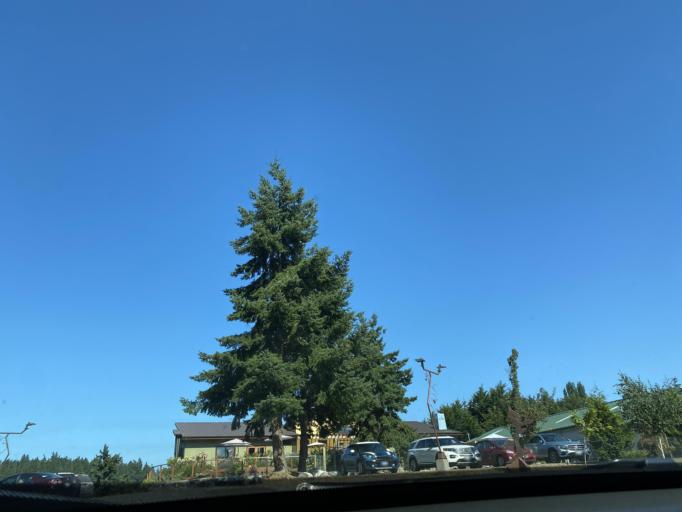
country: US
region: Washington
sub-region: Island County
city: Freeland
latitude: 48.0109
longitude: -122.5338
